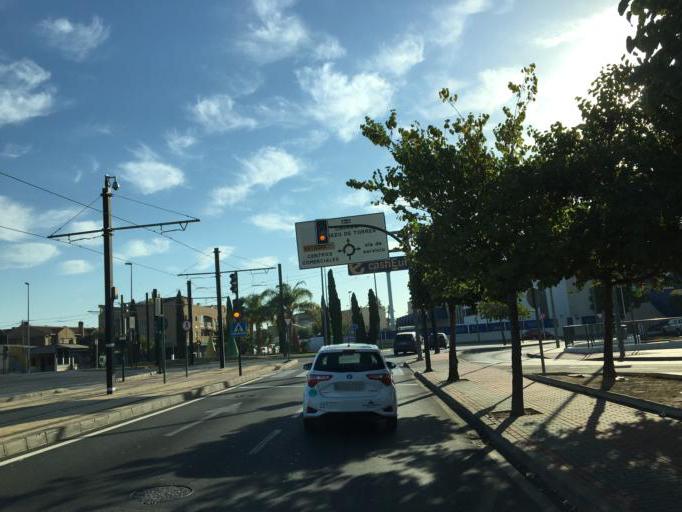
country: ES
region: Murcia
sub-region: Murcia
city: Murcia
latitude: 38.0206
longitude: -1.1390
